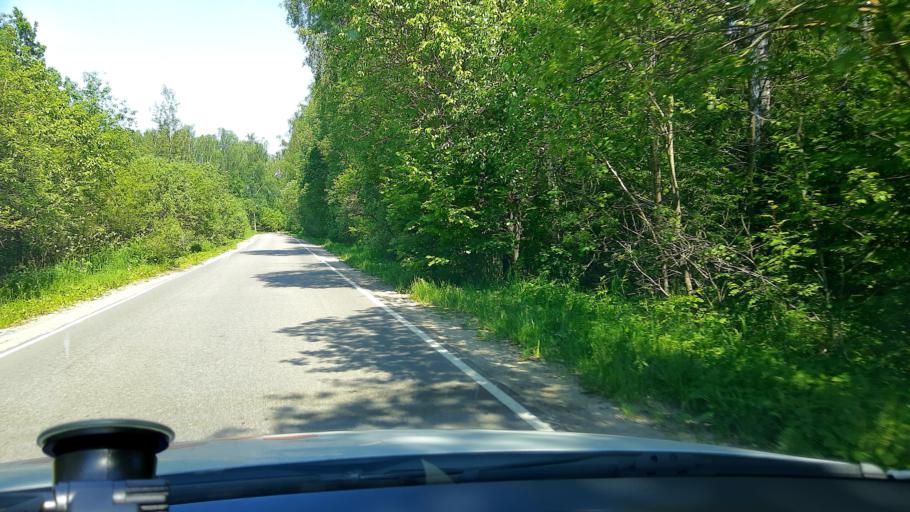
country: RU
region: Moskovskaya
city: Bronnitsy
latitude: 55.4277
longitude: 38.1475
